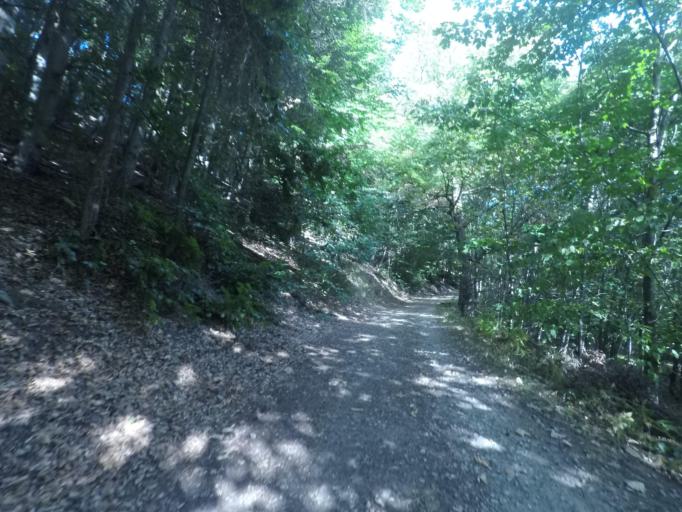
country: LU
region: Luxembourg
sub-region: Canton de Luxembourg
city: Strassen
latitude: 49.6341
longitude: 6.0845
